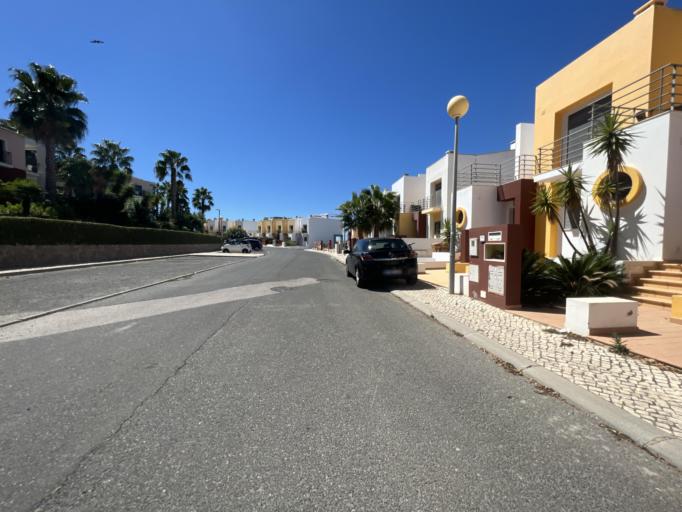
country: PT
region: Faro
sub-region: Portimao
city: Portimao
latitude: 37.1271
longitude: -8.5210
